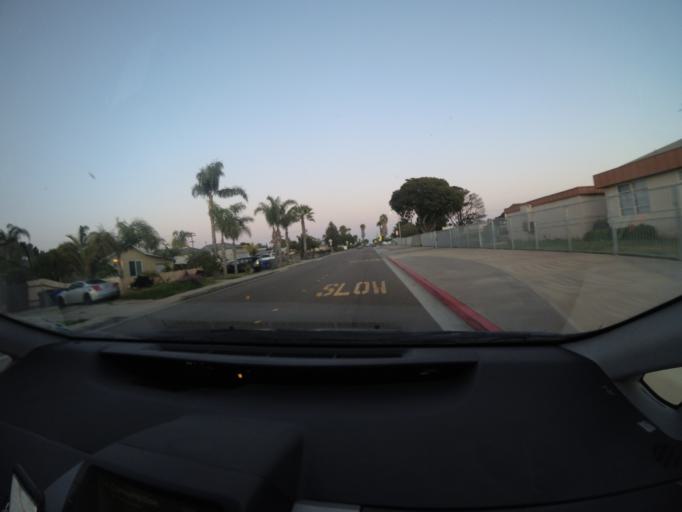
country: US
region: California
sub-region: San Diego County
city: Imperial Beach
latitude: 32.5803
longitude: -117.1203
